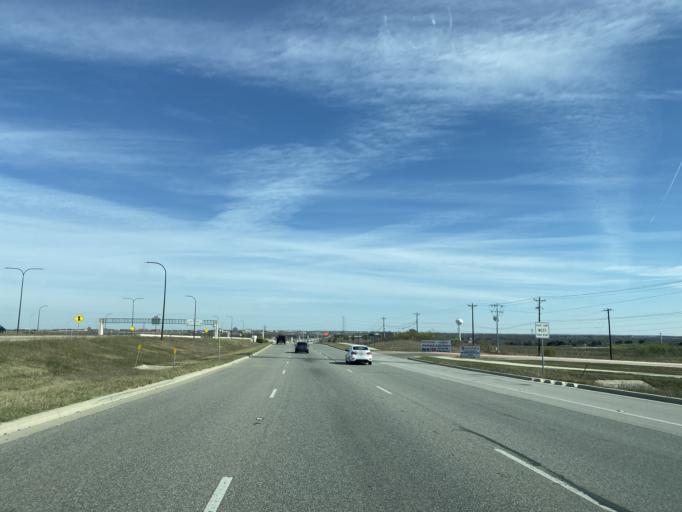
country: US
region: Texas
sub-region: Travis County
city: Manor
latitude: 30.3417
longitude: -97.5865
